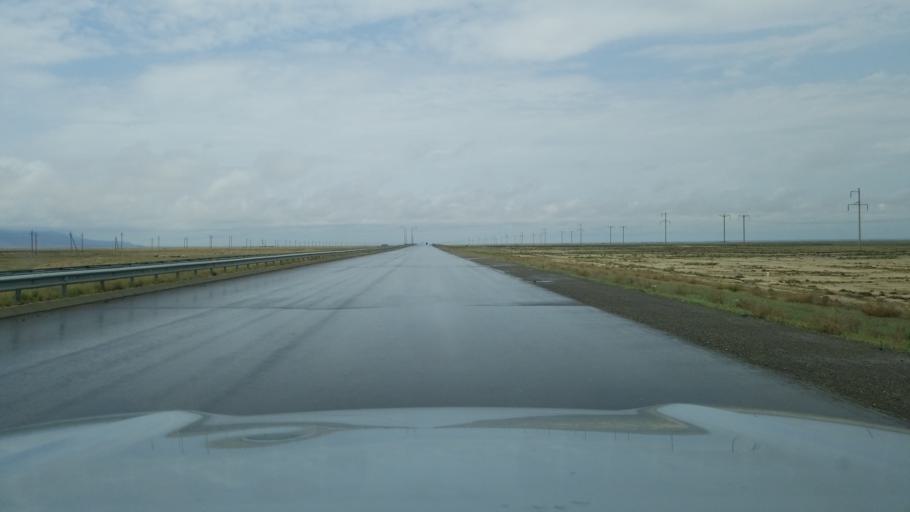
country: TM
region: Balkan
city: Gazanjyk
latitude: 39.1636
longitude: 55.8335
